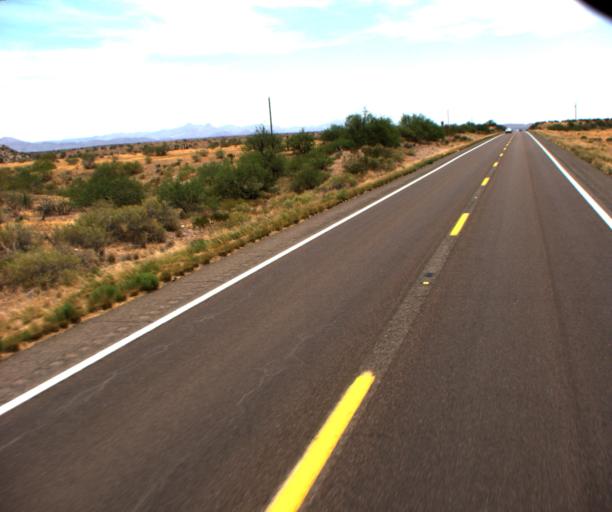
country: US
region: Arizona
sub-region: Graham County
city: Bylas
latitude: 33.2055
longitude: -110.1974
